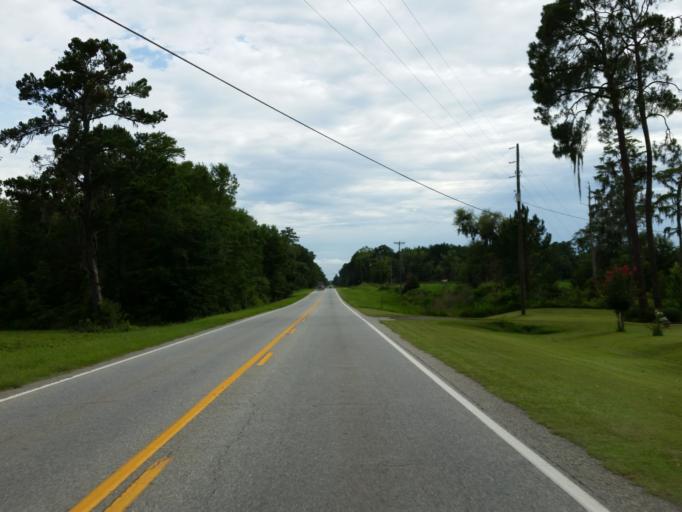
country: US
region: Georgia
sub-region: Lowndes County
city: Valdosta
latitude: 30.7241
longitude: -83.2896
